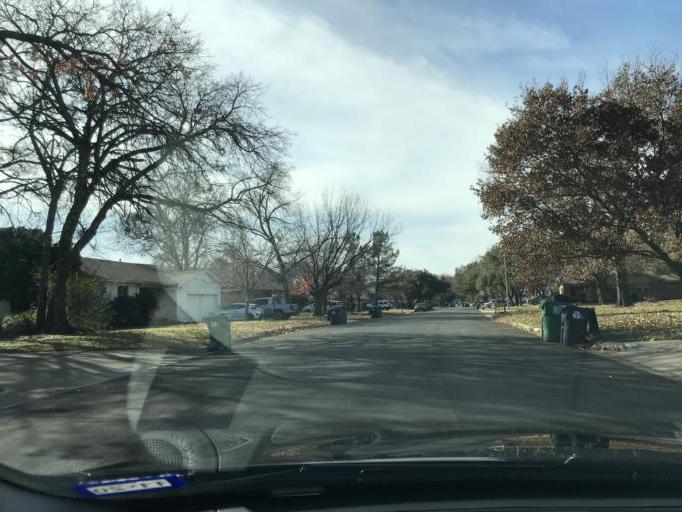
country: US
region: Texas
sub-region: Denton County
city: Denton
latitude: 33.2313
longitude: -97.1457
